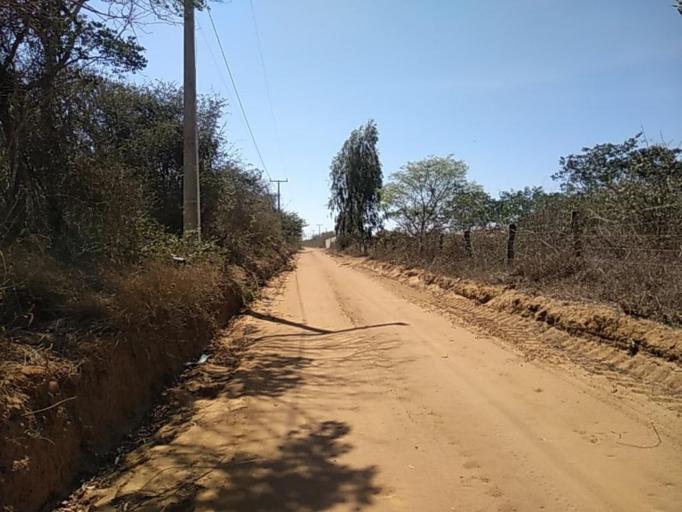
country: BR
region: Bahia
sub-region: Caetite
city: Caetite
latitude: -13.9765
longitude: -42.5165
